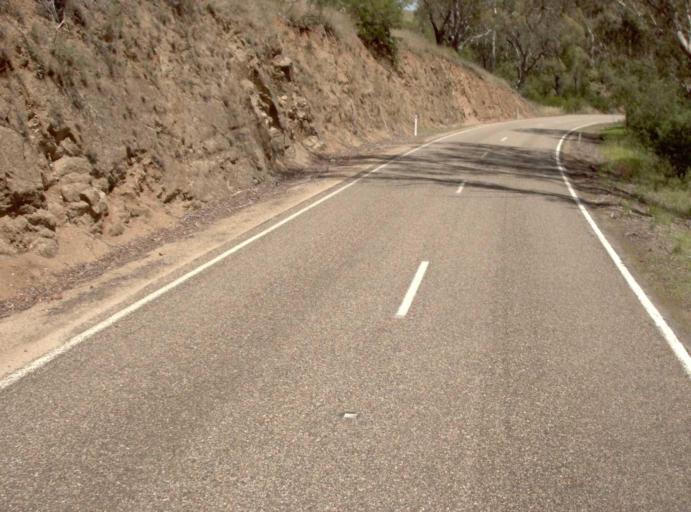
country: AU
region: Victoria
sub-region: East Gippsland
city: Bairnsdale
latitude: -37.3908
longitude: 147.8316
